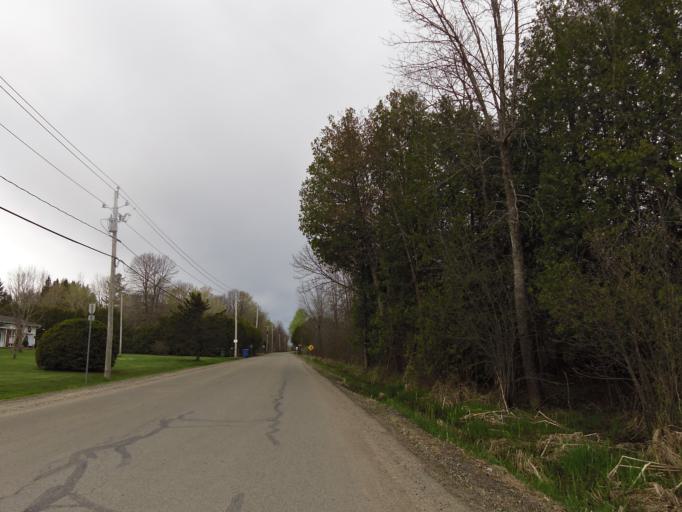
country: CA
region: Ontario
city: Hawkesbury
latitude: 45.6231
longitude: -74.5649
